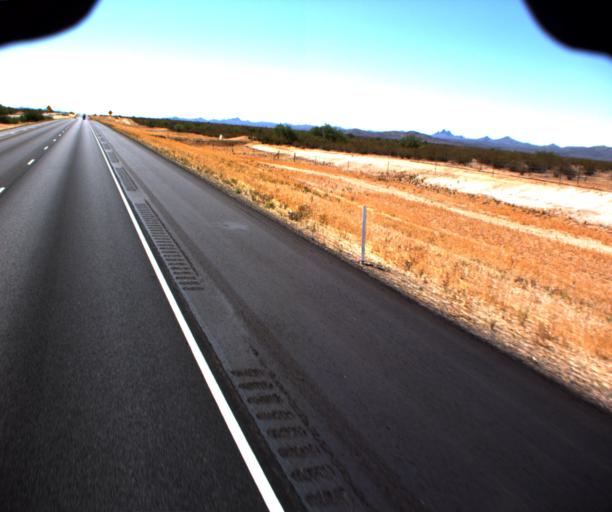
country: US
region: Arizona
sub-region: Yavapai County
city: Congress
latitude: 34.0635
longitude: -112.8651
